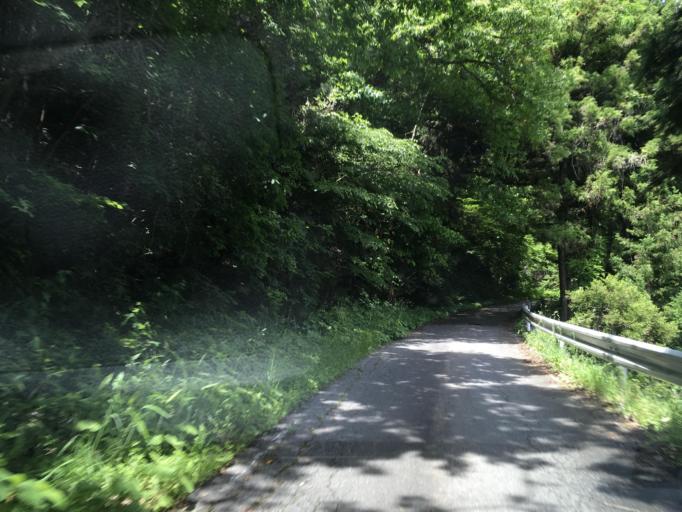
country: JP
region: Iwate
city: Mizusawa
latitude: 39.1241
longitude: 141.2631
